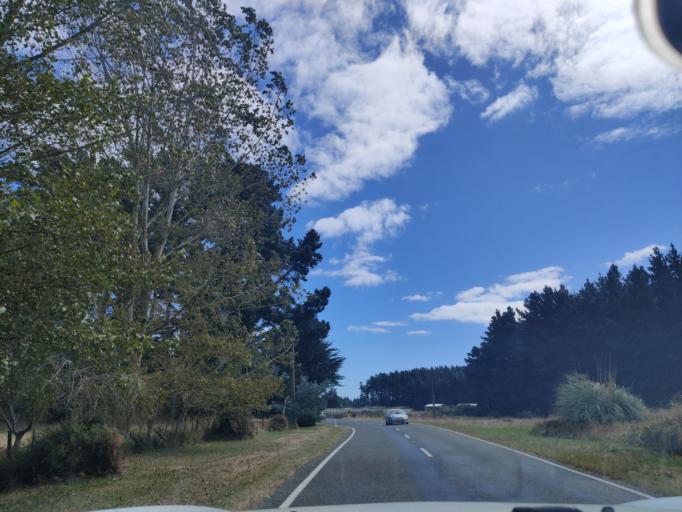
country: NZ
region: Manawatu-Wanganui
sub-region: Horowhenua District
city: Foxton
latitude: -40.3729
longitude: 175.2476
